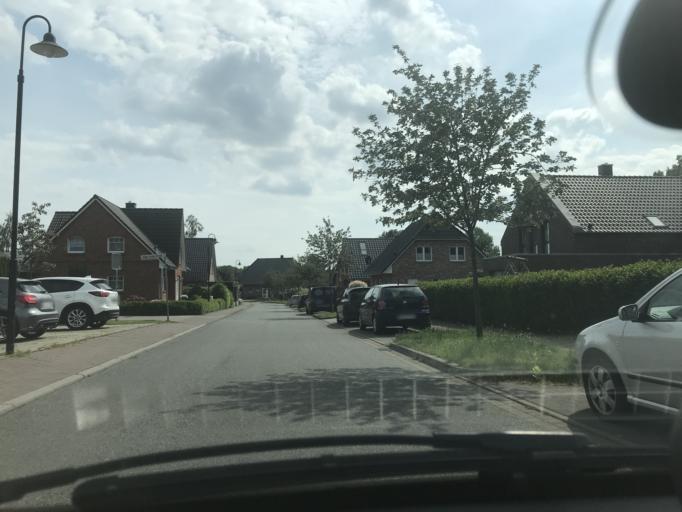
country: DE
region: Schleswig-Holstein
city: Trittau
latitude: 53.6080
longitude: 10.3987
